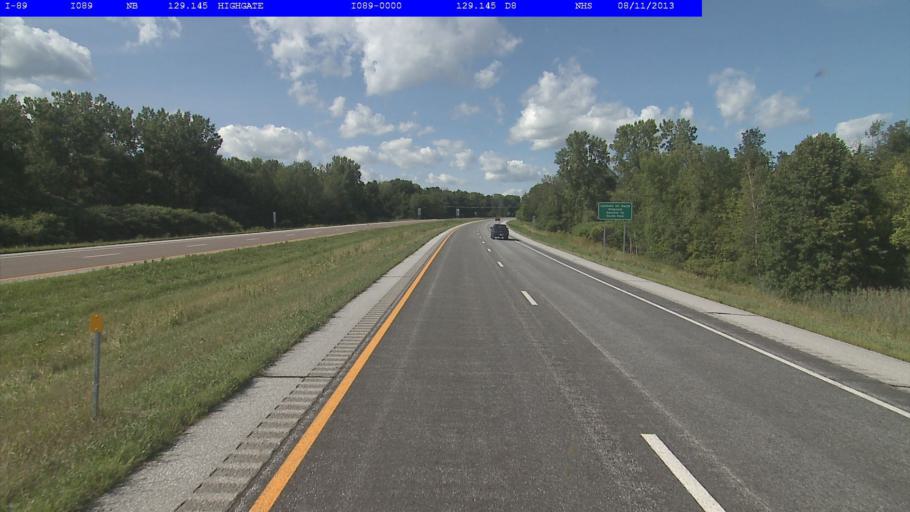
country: US
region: Vermont
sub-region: Franklin County
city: Swanton
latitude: 44.9996
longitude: -73.0865
